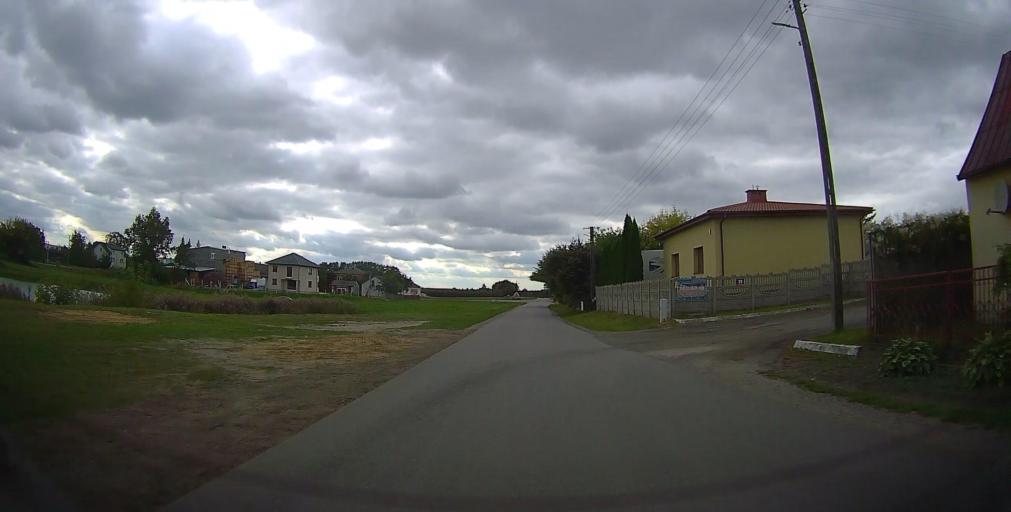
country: PL
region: Masovian Voivodeship
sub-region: Powiat grojecki
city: Goszczyn
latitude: 51.7592
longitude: 20.8747
